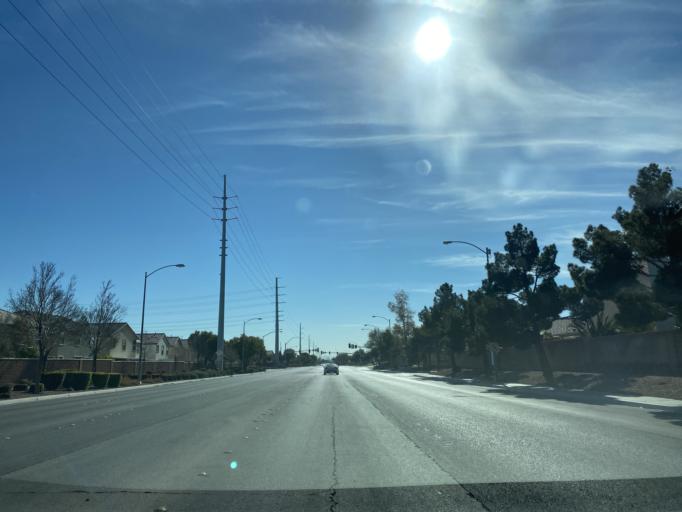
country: US
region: Nevada
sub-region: Clark County
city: North Las Vegas
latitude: 36.2710
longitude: -115.1441
